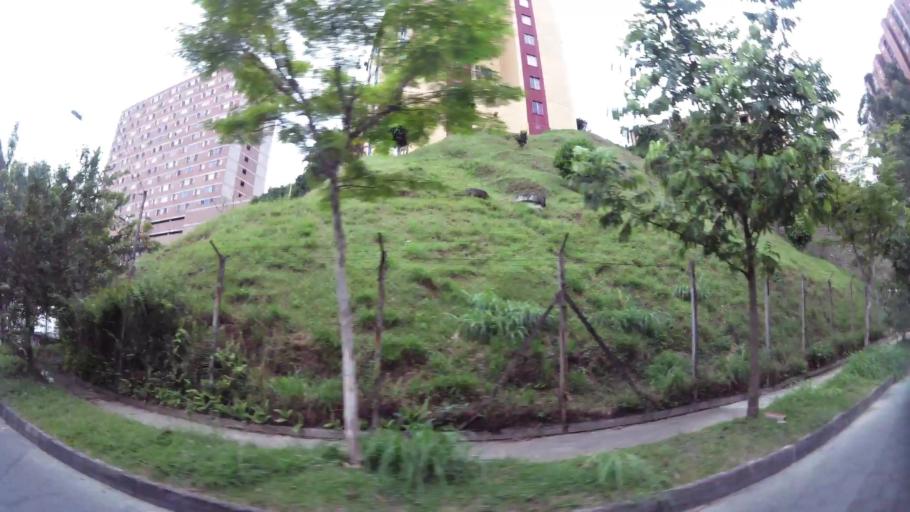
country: CO
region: Antioquia
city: Medellin
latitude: 6.2700
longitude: -75.5998
